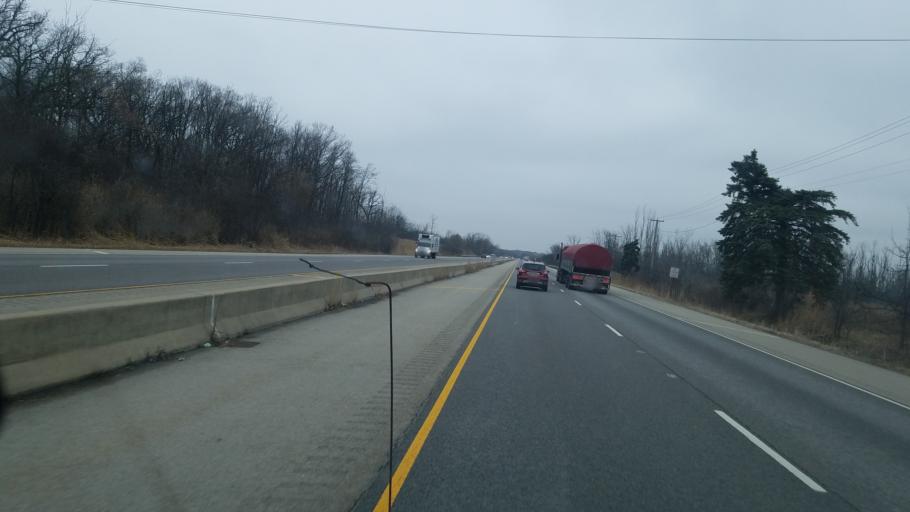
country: US
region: Illinois
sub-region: Lake County
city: Wadsworth
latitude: 42.3979
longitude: -87.9303
